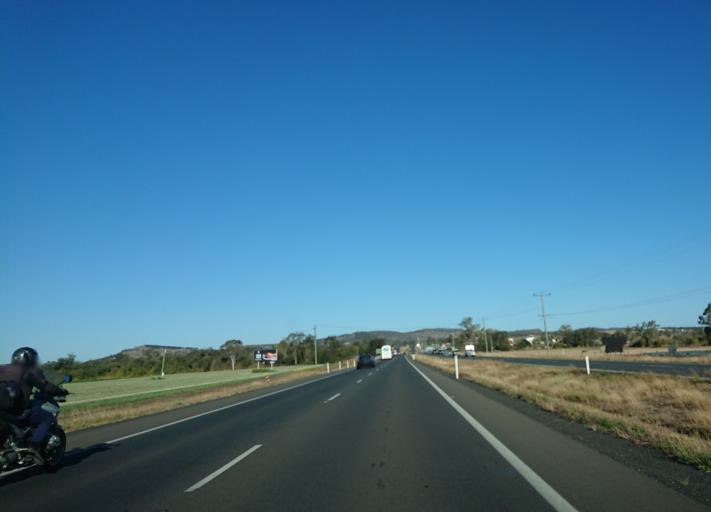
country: AU
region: Queensland
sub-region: Lockyer Valley
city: Gatton
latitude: -27.5499
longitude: 152.3864
